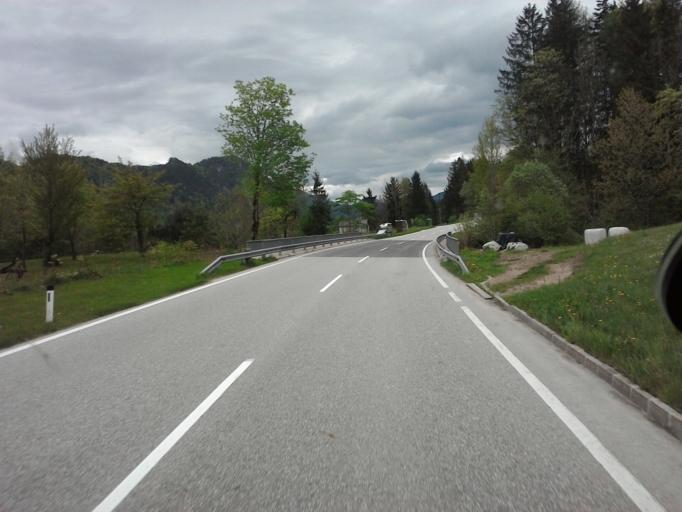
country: AT
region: Upper Austria
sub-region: Politischer Bezirk Kirchdorf an der Krems
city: Rossleithen
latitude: 47.7432
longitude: 14.2579
